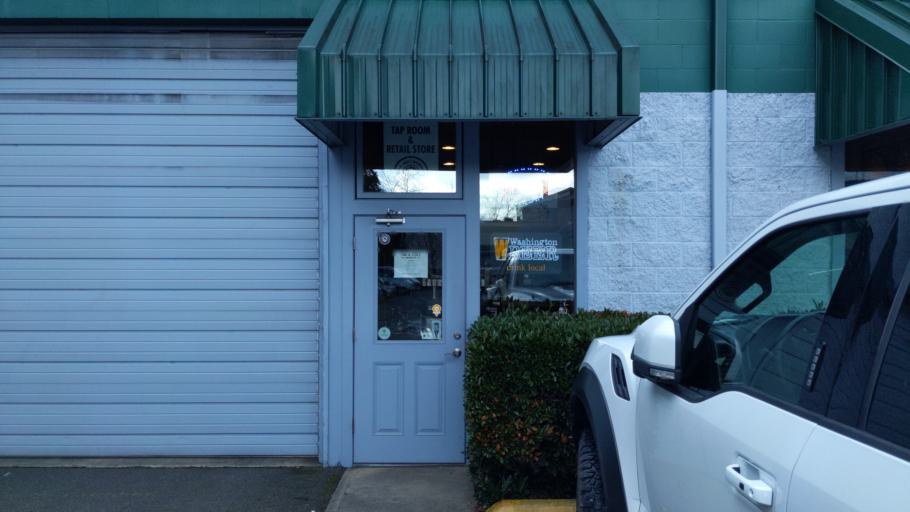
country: US
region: Washington
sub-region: King County
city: Redmond
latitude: 47.6636
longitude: -122.1028
